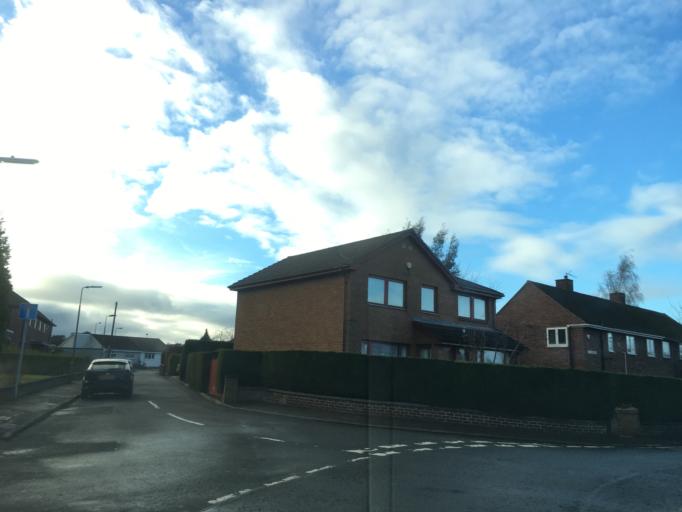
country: GB
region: Scotland
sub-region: Edinburgh
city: Colinton
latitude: 55.9065
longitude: -3.2416
